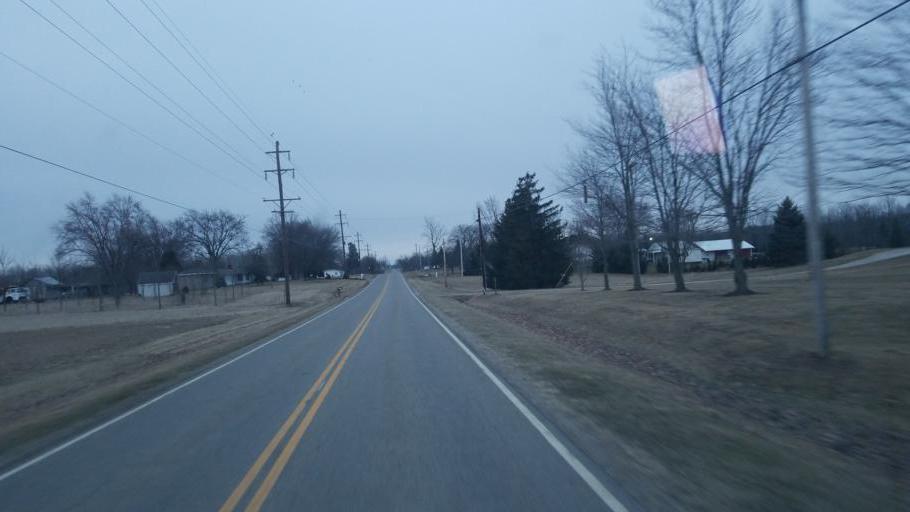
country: US
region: Ohio
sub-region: Defiance County
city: Hicksville
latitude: 41.3234
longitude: -84.7667
